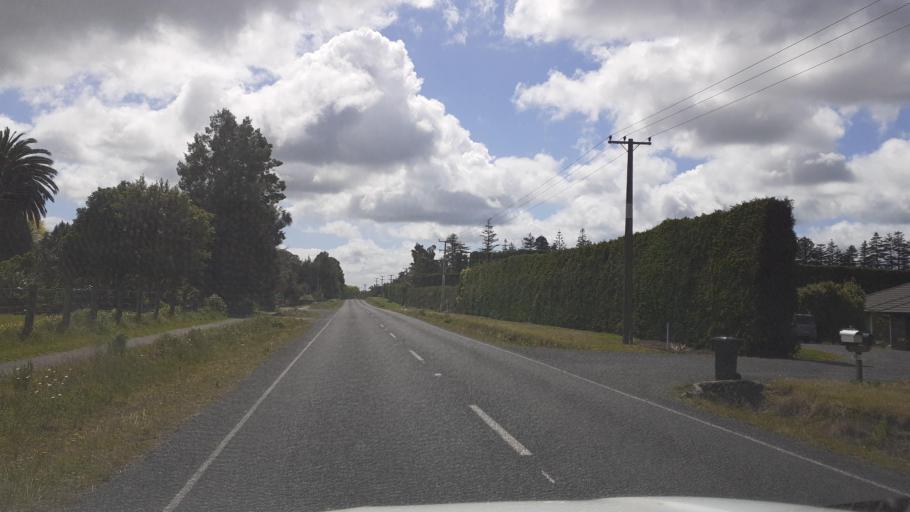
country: NZ
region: Northland
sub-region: Far North District
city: Kerikeri
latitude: -35.2245
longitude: 173.9725
